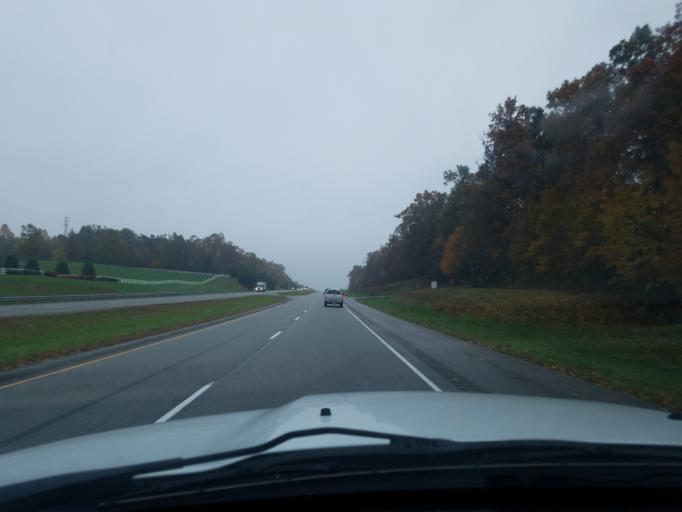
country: US
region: Kentucky
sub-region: Hardin County
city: Elizabethtown
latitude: 37.6394
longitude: -85.8359
